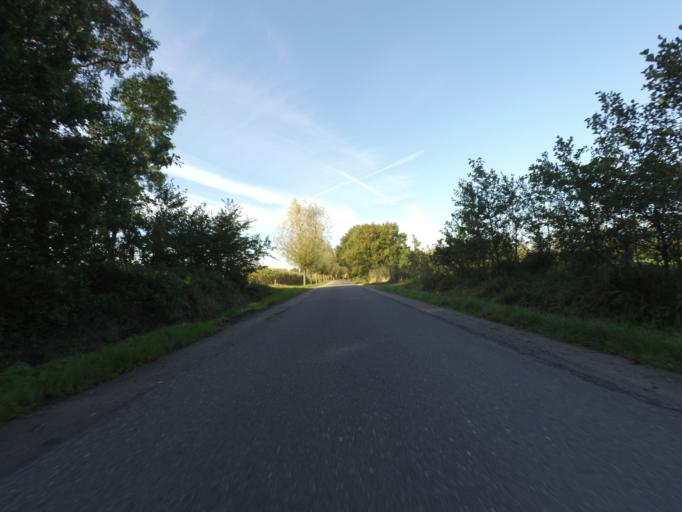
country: NL
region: Gelderland
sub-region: Gemeente Nijkerk
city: Nijkerk
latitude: 52.2248
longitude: 5.5095
